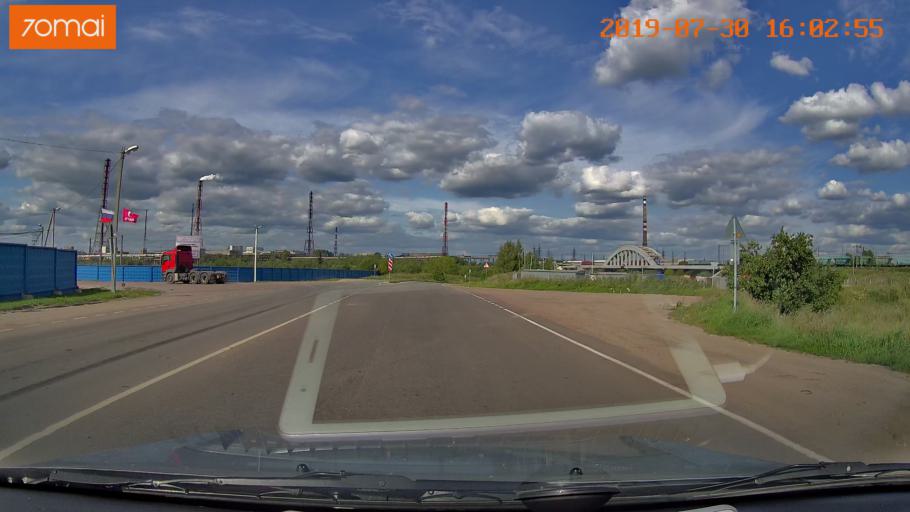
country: RU
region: Moskovskaya
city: Voskresensk
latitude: 55.2891
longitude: 38.6898
